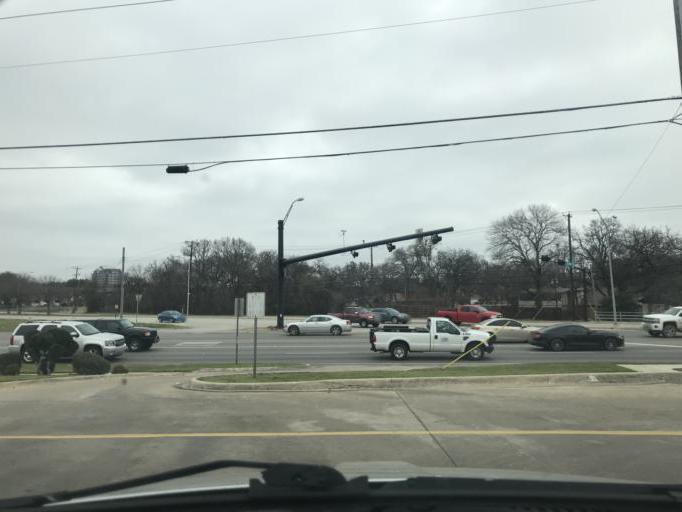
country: US
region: Texas
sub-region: Tarrant County
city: North Richland Hills
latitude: 32.8429
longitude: -97.2021
